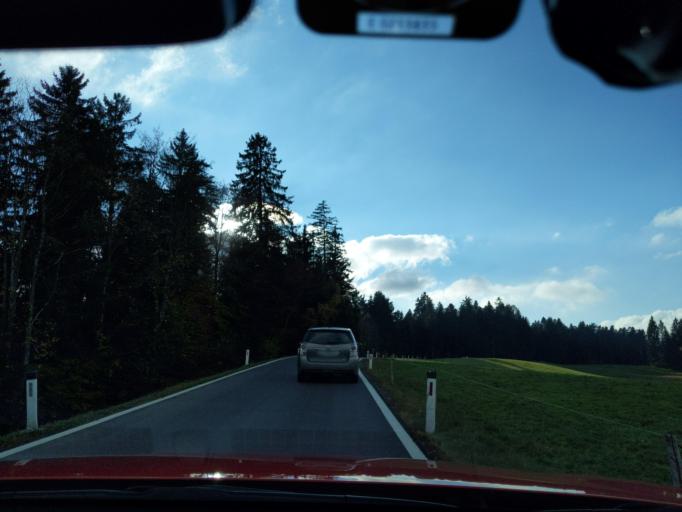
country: AT
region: Vorarlberg
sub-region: Politischer Bezirk Bregenz
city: Moggers
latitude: 47.5685
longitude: 9.8130
